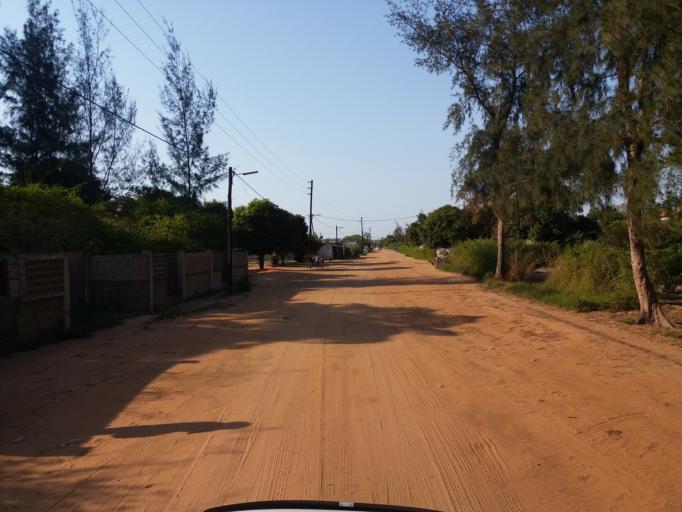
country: MZ
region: Maputo City
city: Maputo
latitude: -25.7679
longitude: 32.6082
